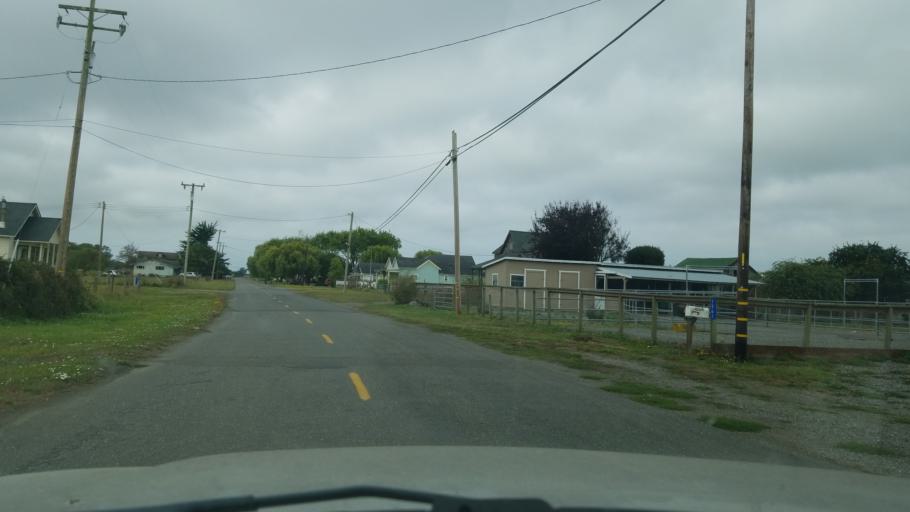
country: US
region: California
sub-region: Humboldt County
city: Ferndale
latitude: 40.5954
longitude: -124.2763
